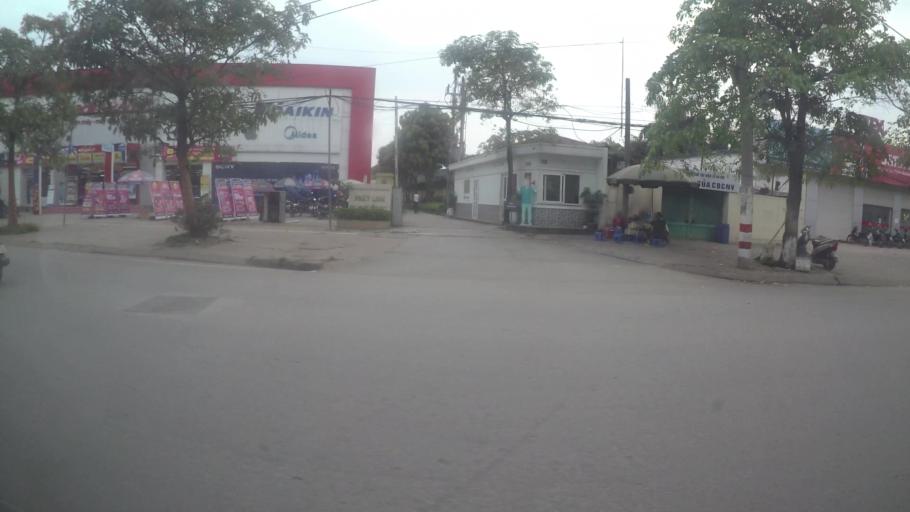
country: VN
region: Ha Noi
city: Cau Dien
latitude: 21.0468
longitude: 105.7477
